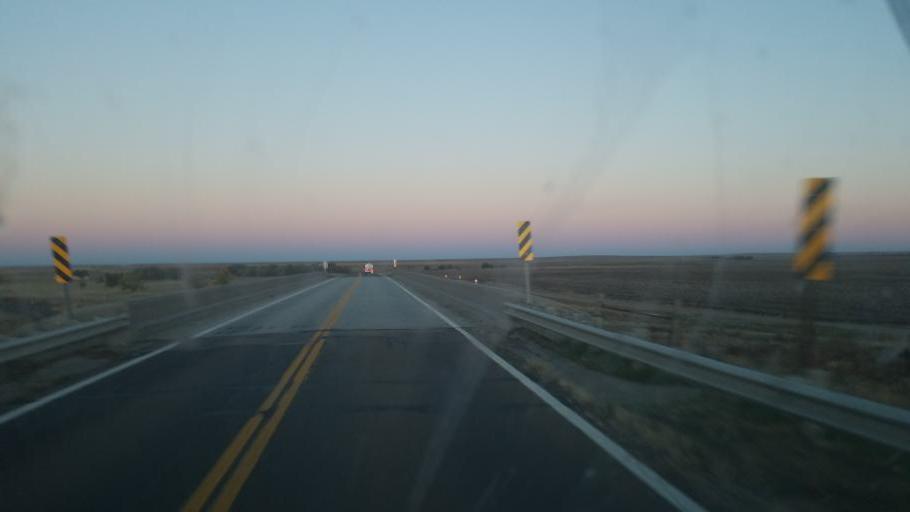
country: US
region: Kansas
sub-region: Wallace County
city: Sharon Springs
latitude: 38.9058
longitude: -101.6176
